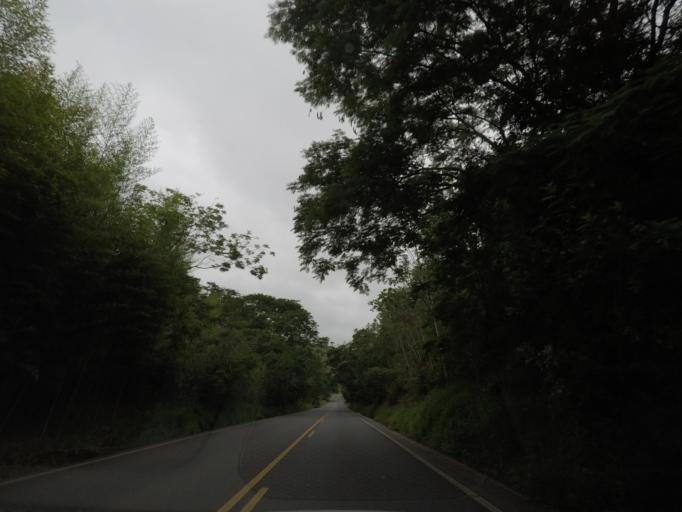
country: BR
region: Sao Paulo
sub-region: Cunha
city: Cunha
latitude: -22.9454
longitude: -45.0609
